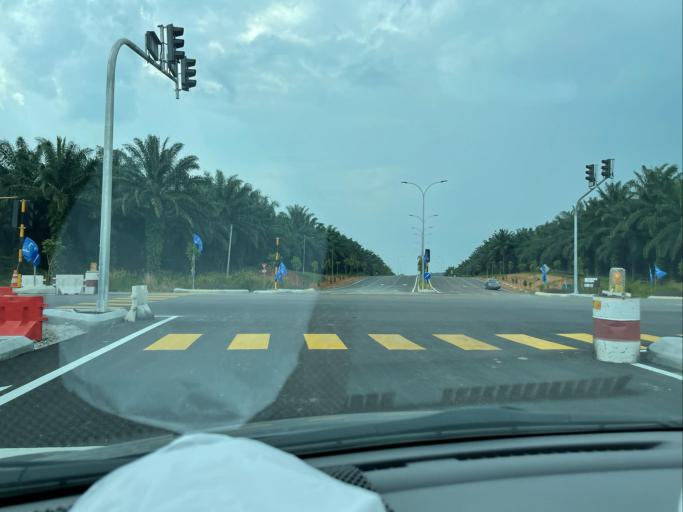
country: MY
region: Melaka
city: Kampung Ayer Keroh
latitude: 2.3176
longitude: 102.2489
